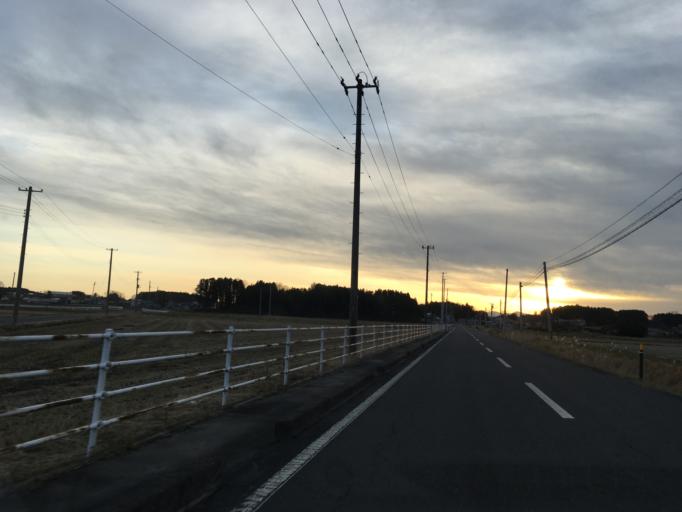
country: JP
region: Miyagi
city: Kogota
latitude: 38.6470
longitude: 141.0572
